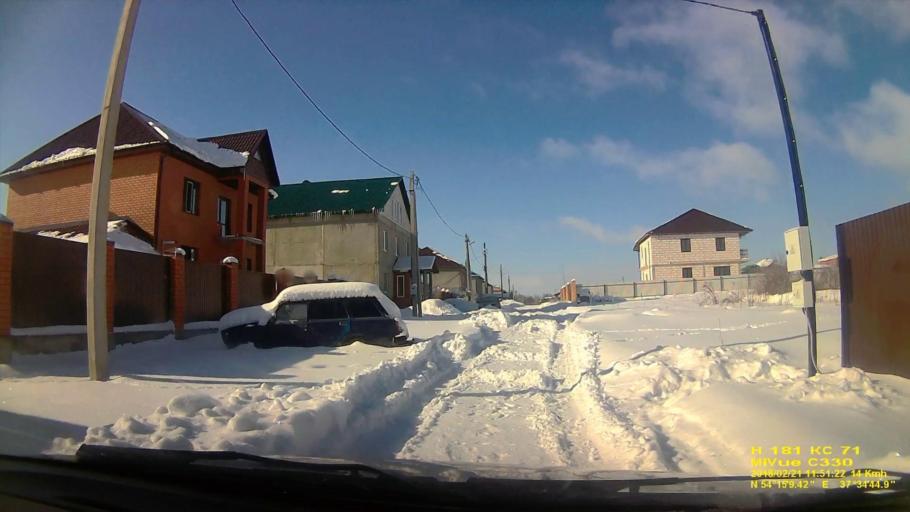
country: RU
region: Tula
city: Gorelki
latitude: 54.2526
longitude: 37.5790
